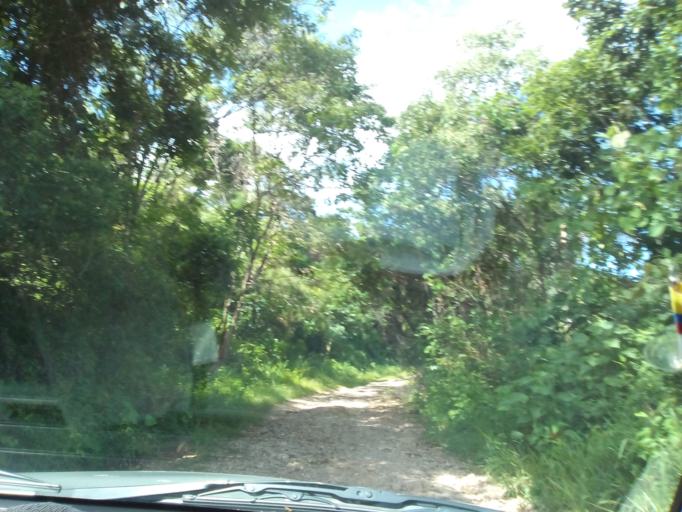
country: CO
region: Casanare
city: Nunchia
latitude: 5.6252
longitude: -72.2726
